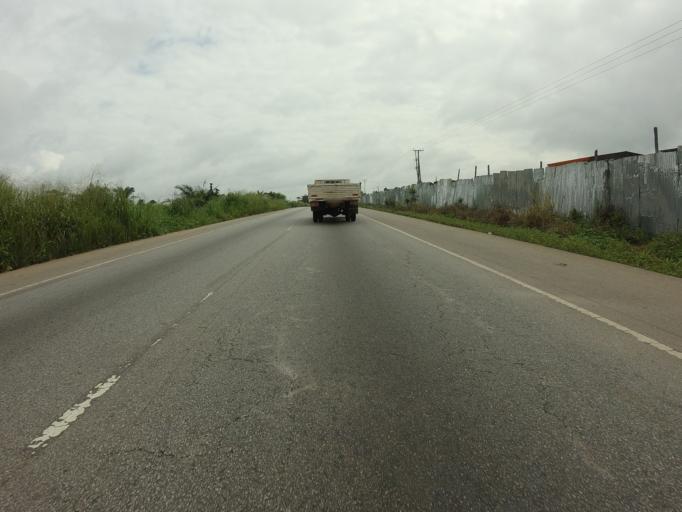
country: GH
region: Ashanti
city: Tafo
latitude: 6.9798
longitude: -1.6871
